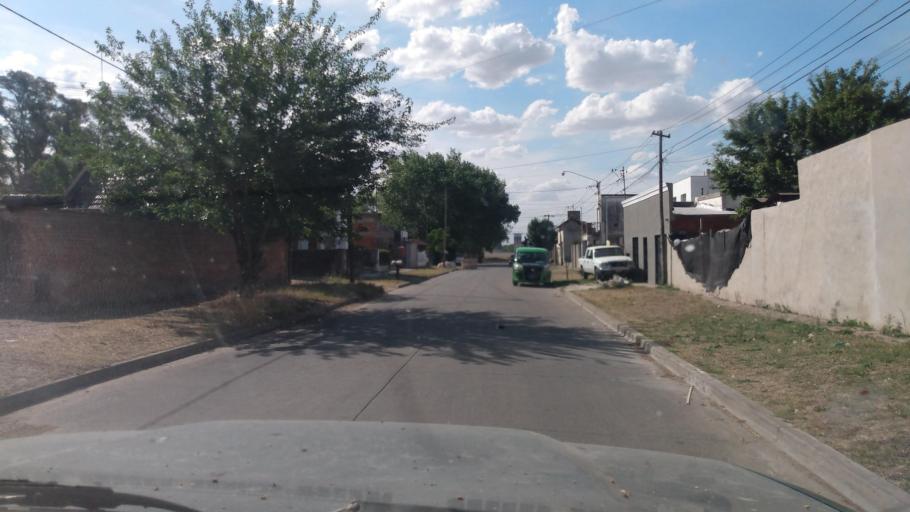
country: AR
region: Buenos Aires
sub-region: Partido de Lujan
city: Lujan
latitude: -34.5531
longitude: -59.1101
